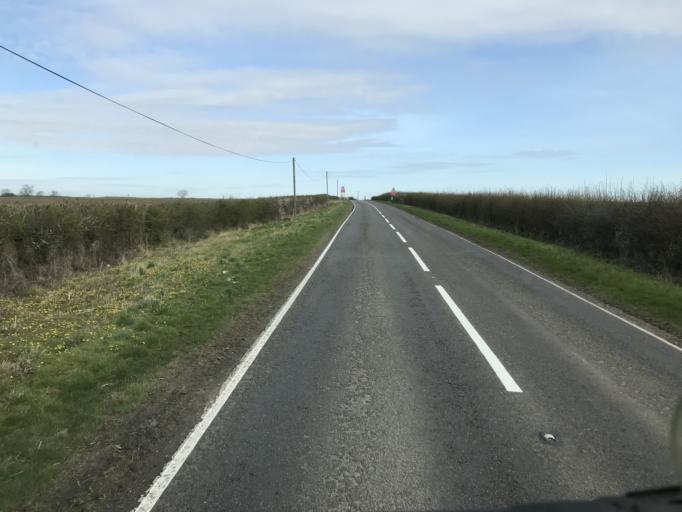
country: GB
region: England
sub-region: Lincolnshire
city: Market Rasen
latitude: 53.3921
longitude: -0.4054
